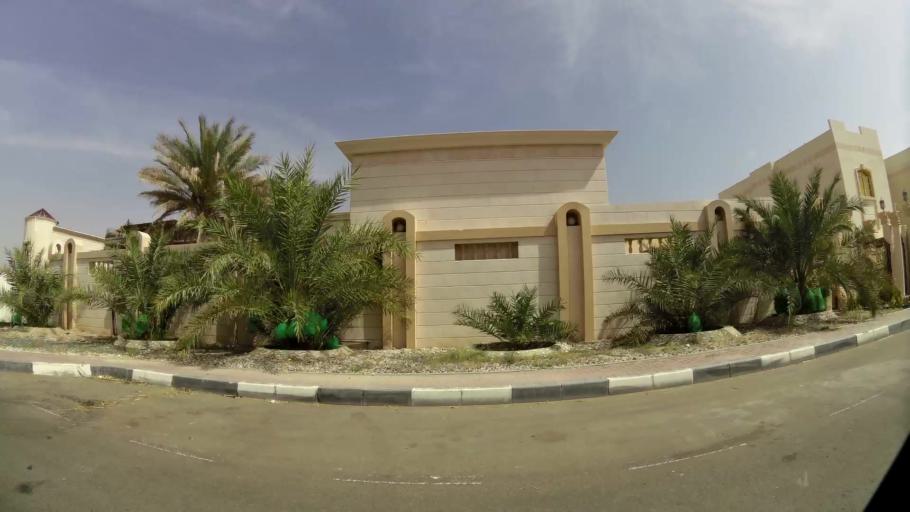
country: AE
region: Abu Dhabi
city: Al Ain
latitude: 24.1632
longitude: 55.6773
